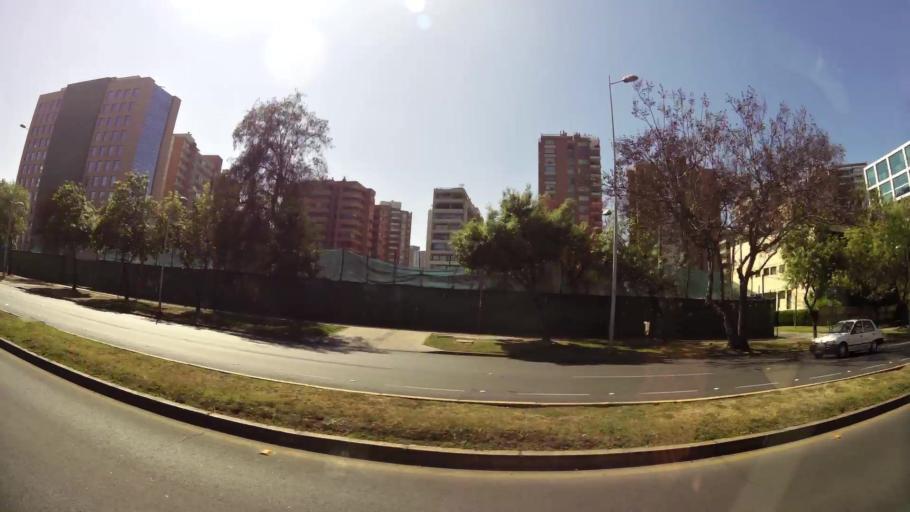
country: CL
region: Santiago Metropolitan
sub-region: Provincia de Santiago
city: Villa Presidente Frei, Nunoa, Santiago, Chile
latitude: -33.4063
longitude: -70.5682
